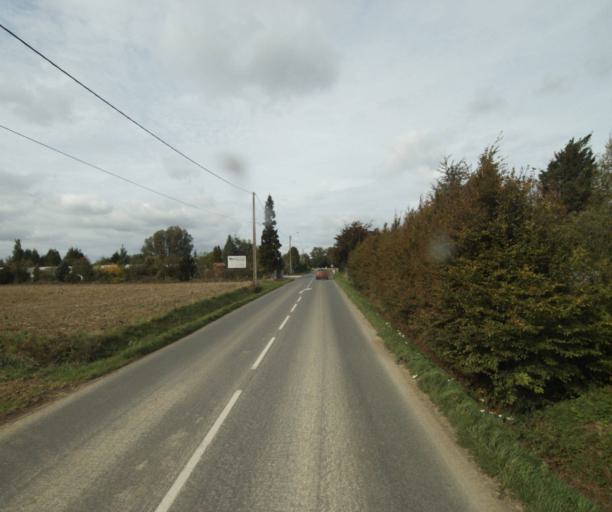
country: FR
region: Nord-Pas-de-Calais
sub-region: Departement du Nord
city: Bois-Grenier
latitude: 50.6377
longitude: 2.8873
